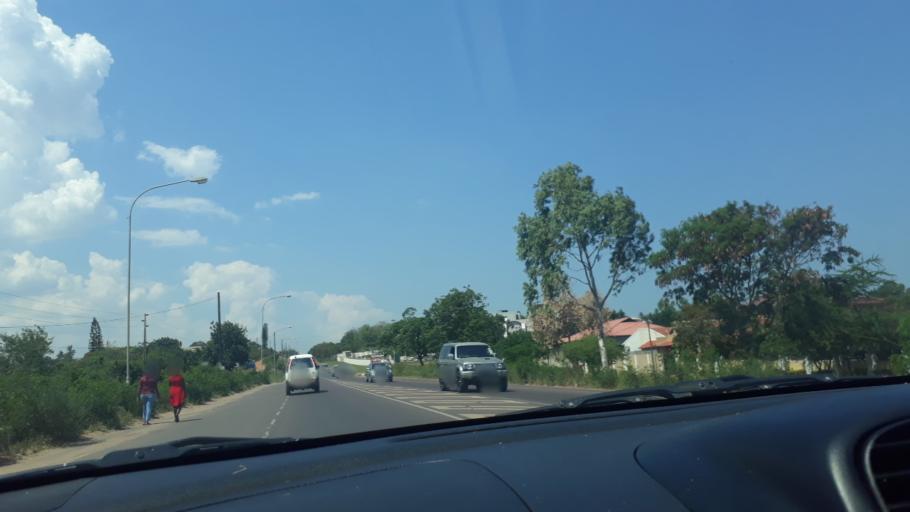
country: MZ
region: Maputo
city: Matola
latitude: -25.9668
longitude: 32.4444
